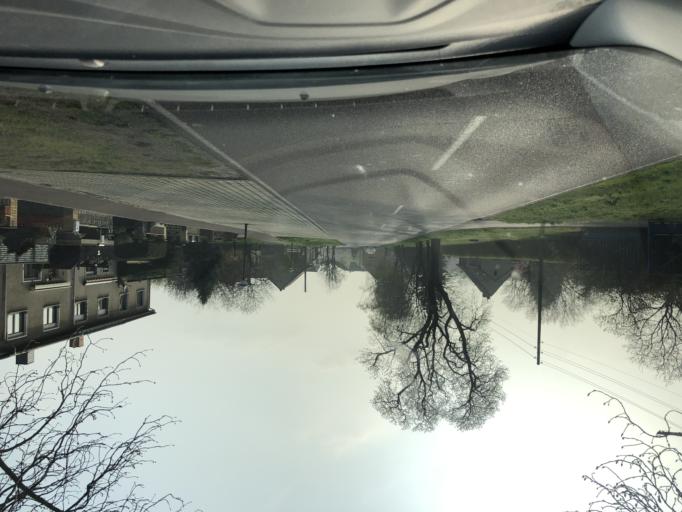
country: DE
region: Saxony-Anhalt
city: Zorbig
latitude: 51.6012
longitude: 12.1287
